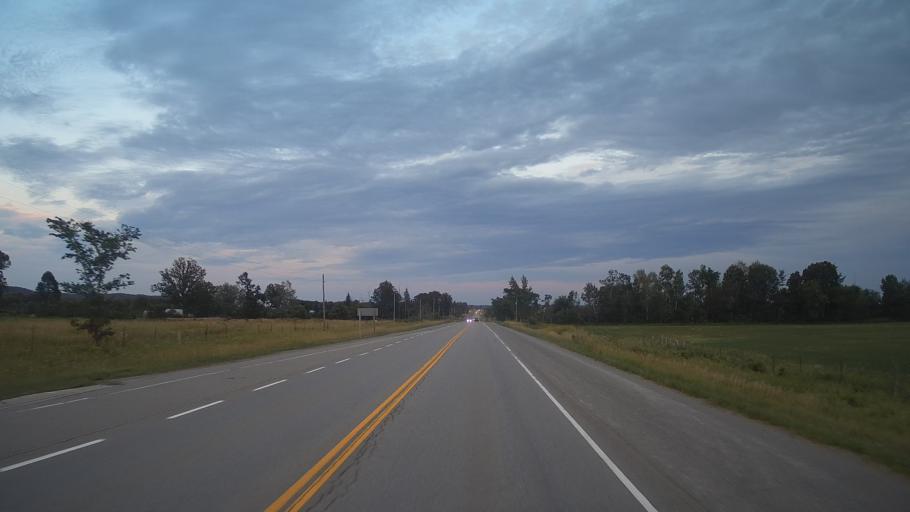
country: CA
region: Ontario
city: Pembroke
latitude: 45.6992
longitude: -76.9640
